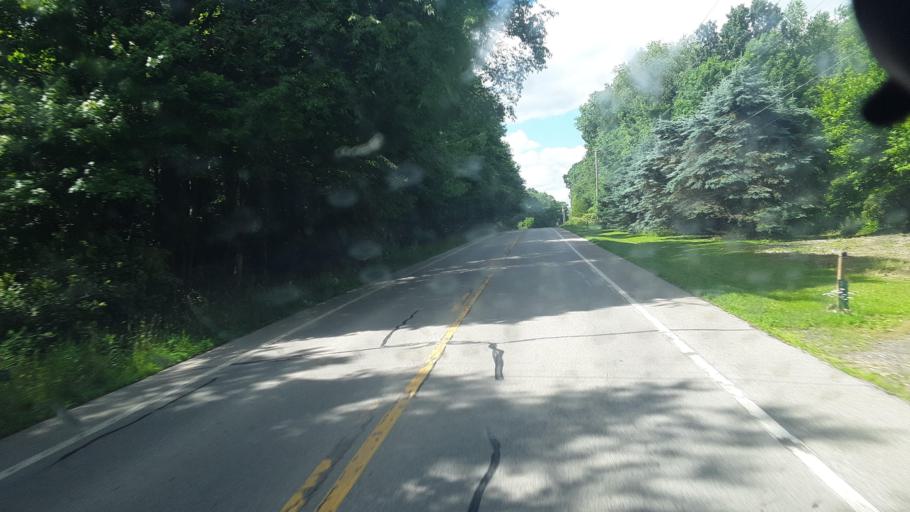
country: US
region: Pennsylvania
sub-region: Butler County
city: Slippery Rock
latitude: 41.0355
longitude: -80.1941
